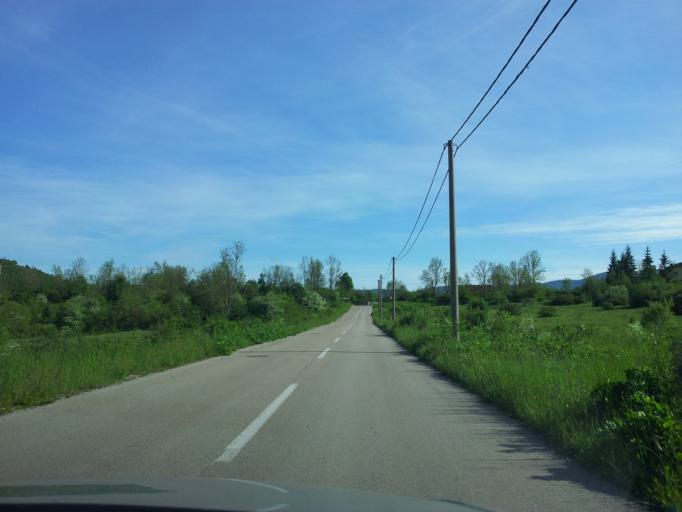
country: HR
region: Zadarska
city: Obrovac
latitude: 44.3842
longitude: 15.6780
